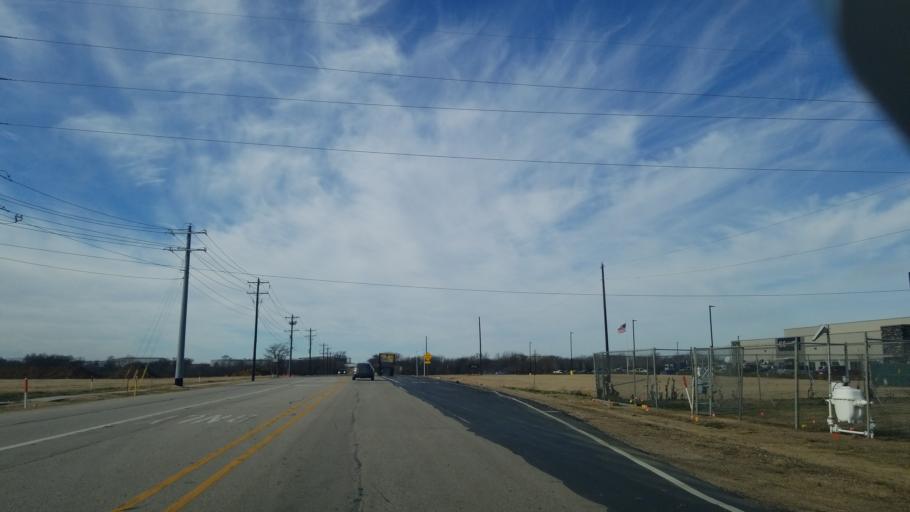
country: US
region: Texas
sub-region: Denton County
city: Denton
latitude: 33.2018
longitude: -97.1826
